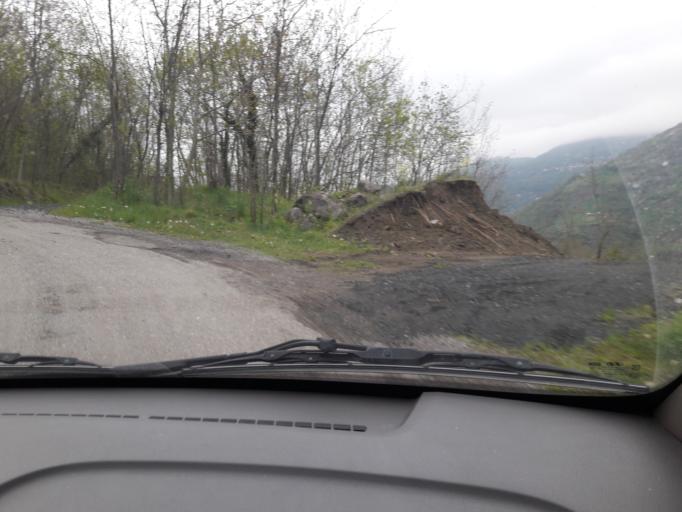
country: TR
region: Trabzon
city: Duzkoy
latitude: 40.9276
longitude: 39.4835
